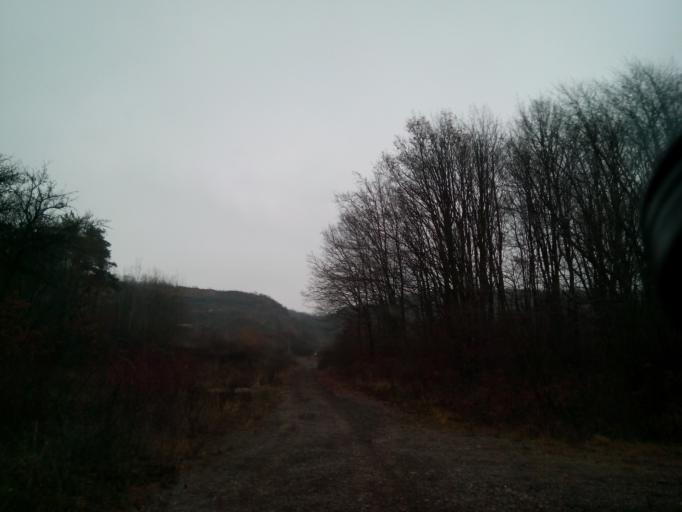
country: SK
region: Kosicky
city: Kosice
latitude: 48.6923
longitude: 21.4532
